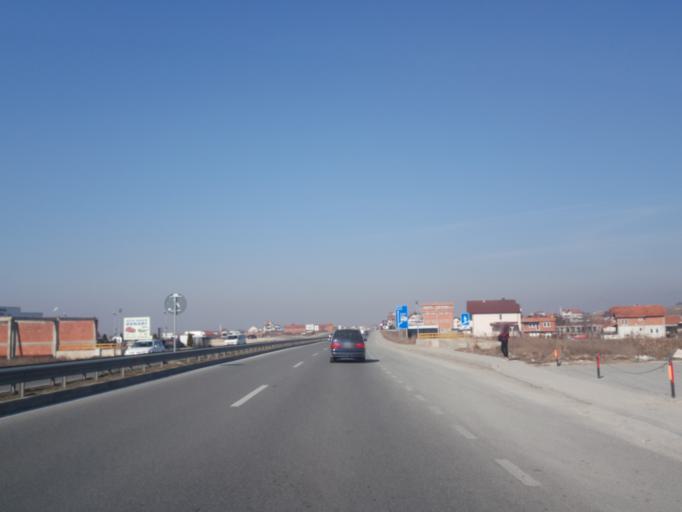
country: XK
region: Pristina
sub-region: Komuna e Obiliqit
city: Obiliq
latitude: 42.7499
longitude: 21.0424
